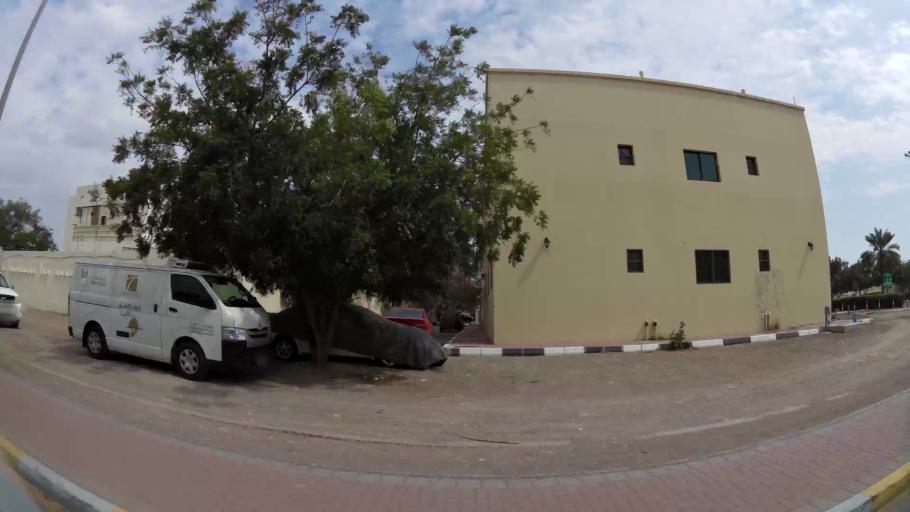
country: AE
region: Abu Dhabi
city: Al Ain
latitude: 24.2151
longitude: 55.7844
